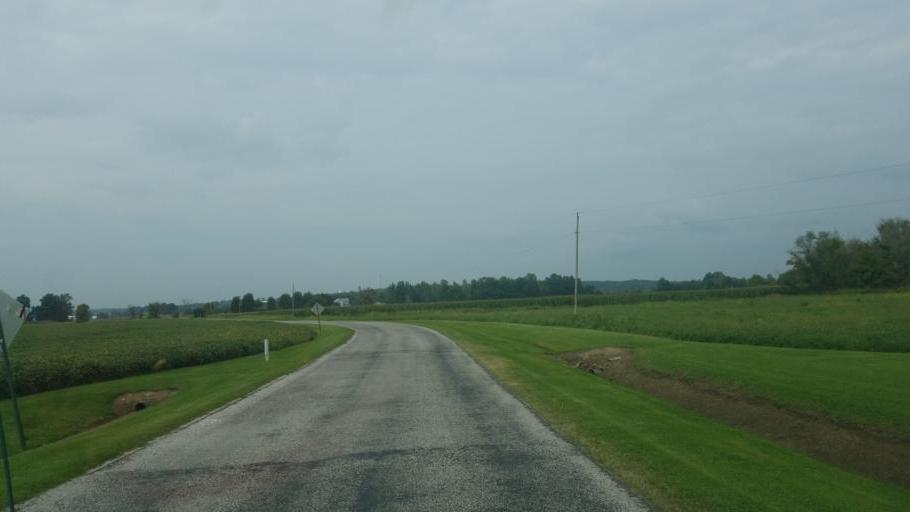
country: US
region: Ohio
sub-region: Wayne County
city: Rittman
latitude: 40.9466
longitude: -81.8123
